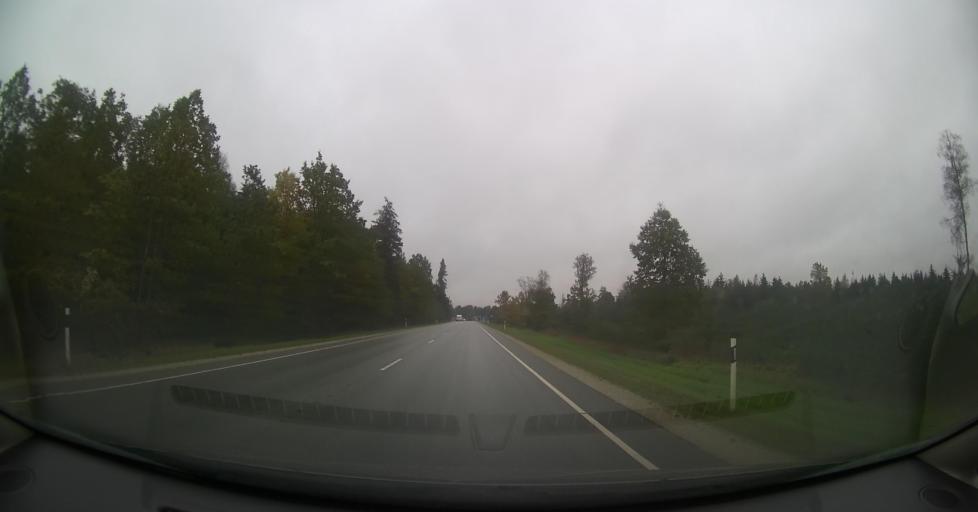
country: EE
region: Jaervamaa
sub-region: Paide linn
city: Paide
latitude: 58.9795
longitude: 25.6147
